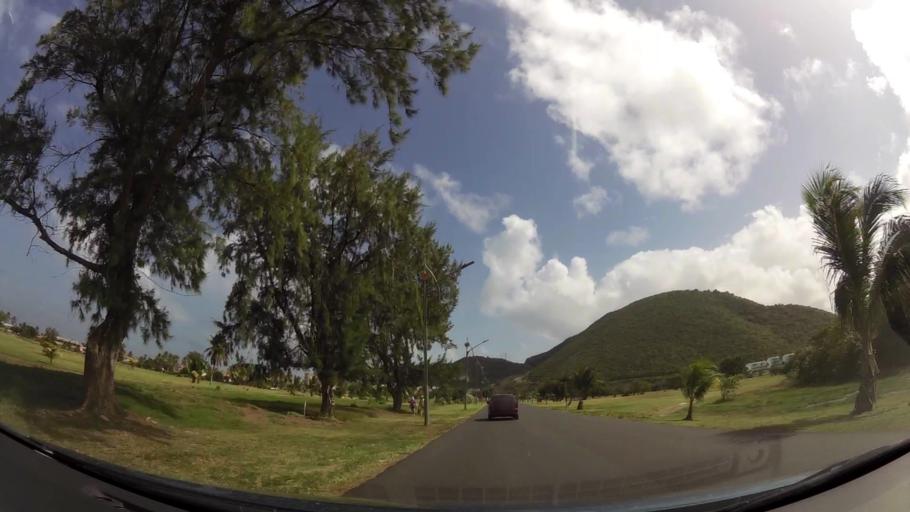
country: KN
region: Saint George Basseterre
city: Basseterre
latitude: 17.2848
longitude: -62.6883
